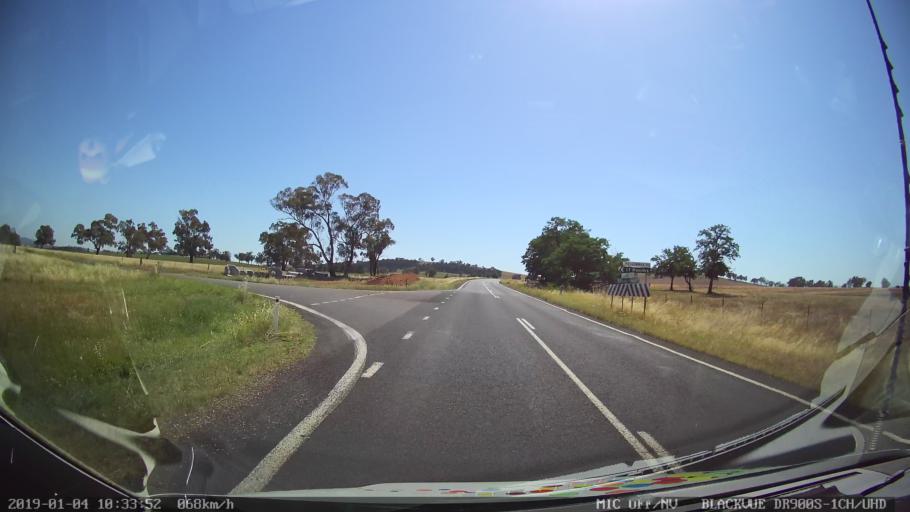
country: AU
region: New South Wales
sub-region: Cabonne
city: Canowindra
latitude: -33.3175
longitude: 148.6554
